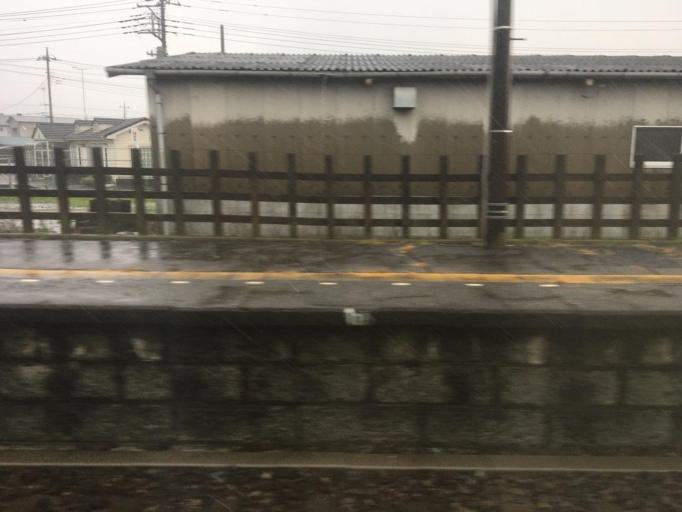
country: JP
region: Gunma
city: Tatebayashi
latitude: 36.2739
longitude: 139.5000
